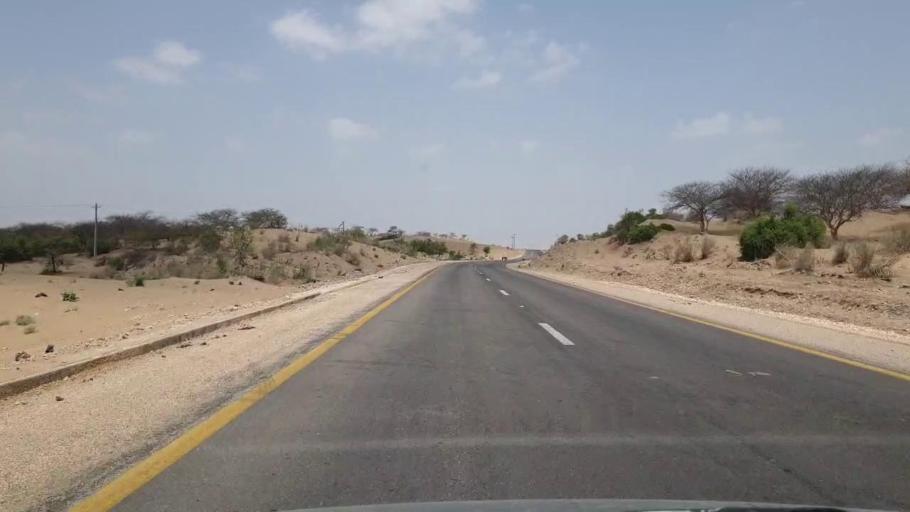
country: PK
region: Sindh
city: Mithi
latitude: 24.7988
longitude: 69.7407
